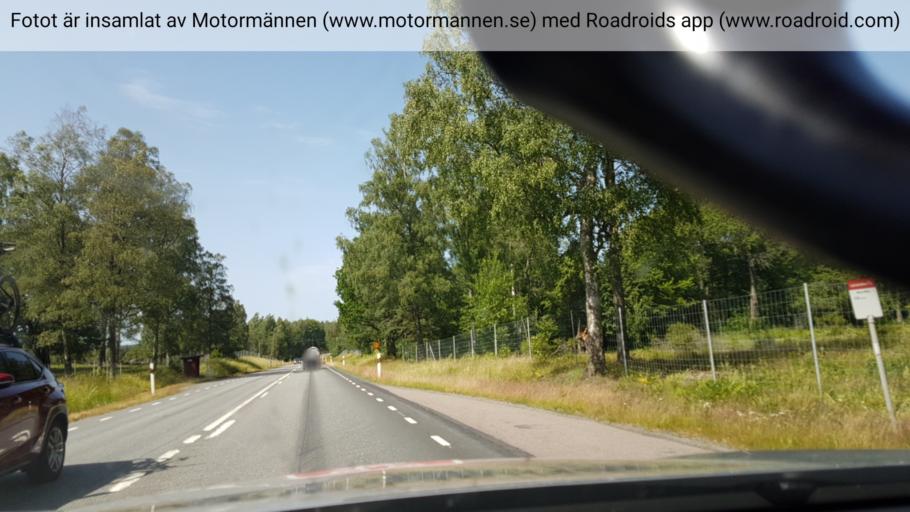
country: SE
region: Joenkoeping
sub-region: Eksjo Kommun
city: Eksjoe
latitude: 57.7205
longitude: 14.9394
